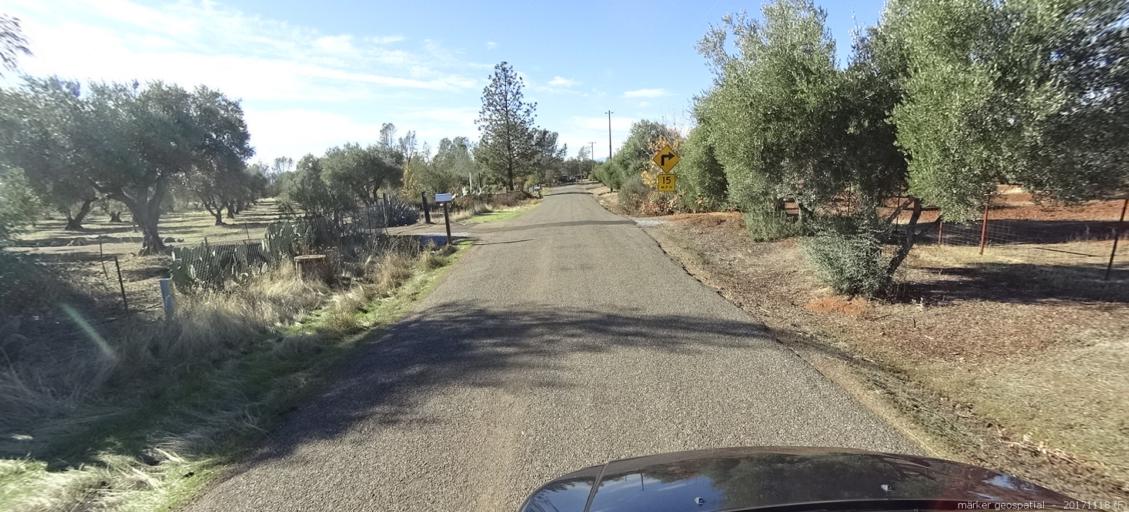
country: US
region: California
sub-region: Shasta County
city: Anderson
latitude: 40.4391
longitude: -122.4341
